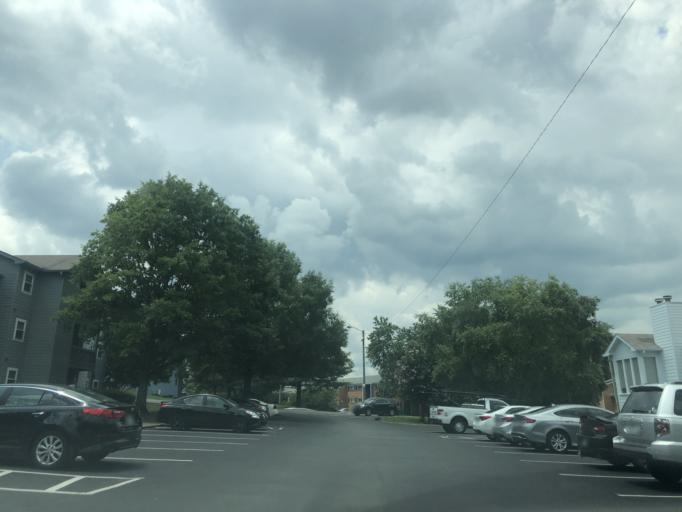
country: US
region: Tennessee
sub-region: Rutherford County
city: La Vergne
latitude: 36.0479
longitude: -86.6669
